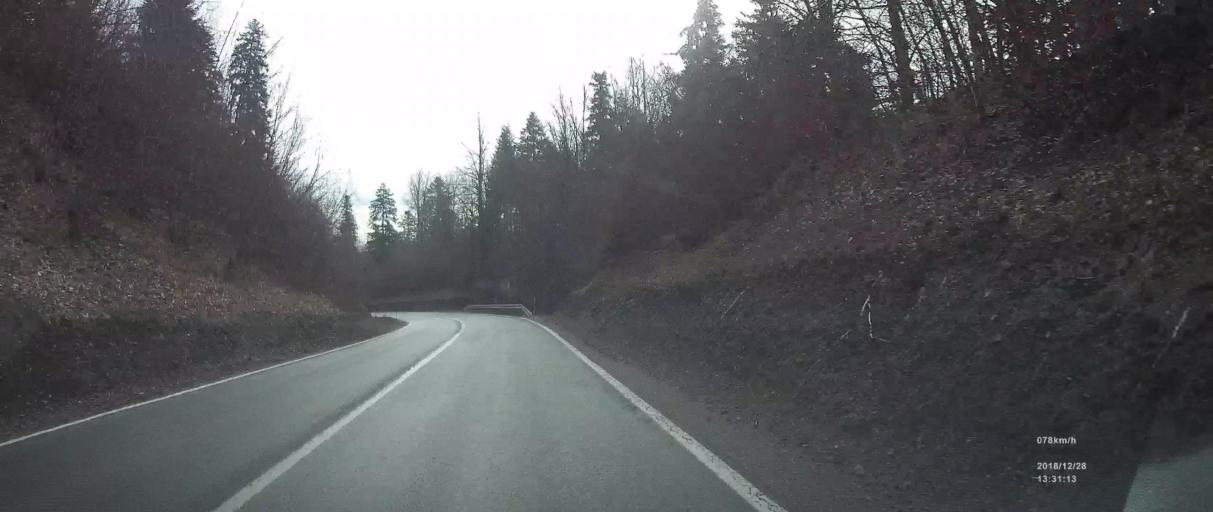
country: HR
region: Primorsko-Goranska
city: Hreljin
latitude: 45.3513
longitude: 14.6488
